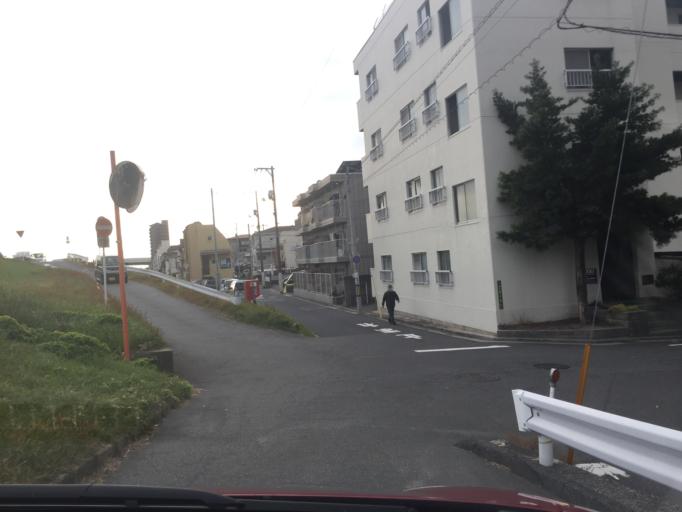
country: JP
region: Hiroshima
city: Hiroshima-shi
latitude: 34.3863
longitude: 132.4218
